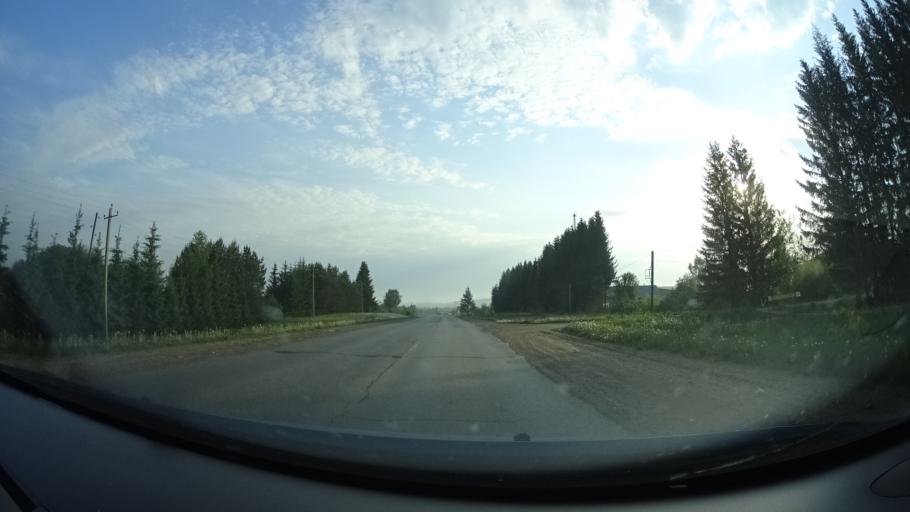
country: RU
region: Perm
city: Barda
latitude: 56.9411
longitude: 55.5880
